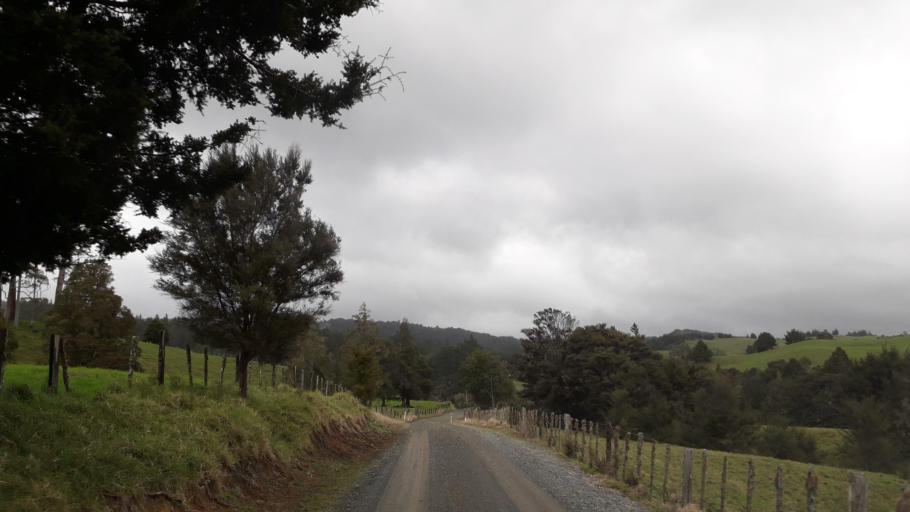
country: NZ
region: Northland
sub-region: Far North District
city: Waimate North
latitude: -35.1551
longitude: 173.7151
